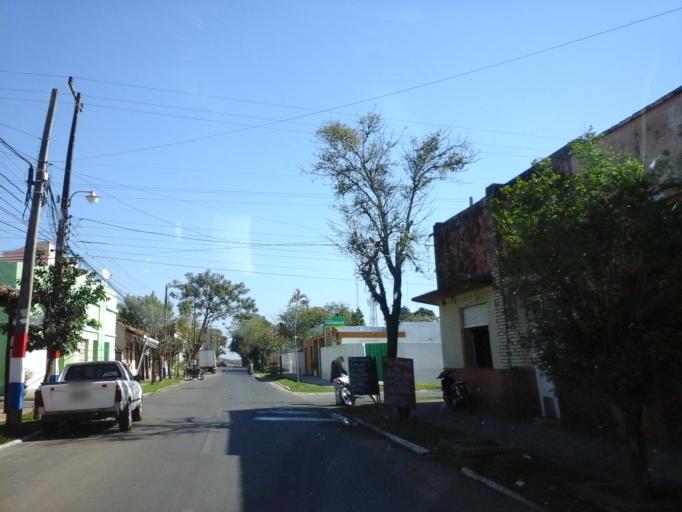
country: PY
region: Neembucu
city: Pilar
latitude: -26.8550
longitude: -58.3092
